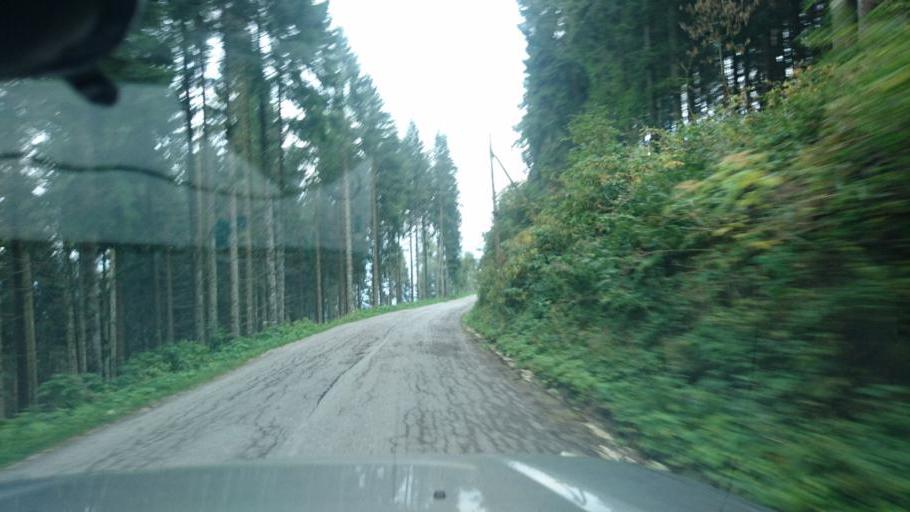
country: IT
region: Veneto
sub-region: Provincia di Vicenza
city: Enego
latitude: 45.9377
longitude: 11.6828
